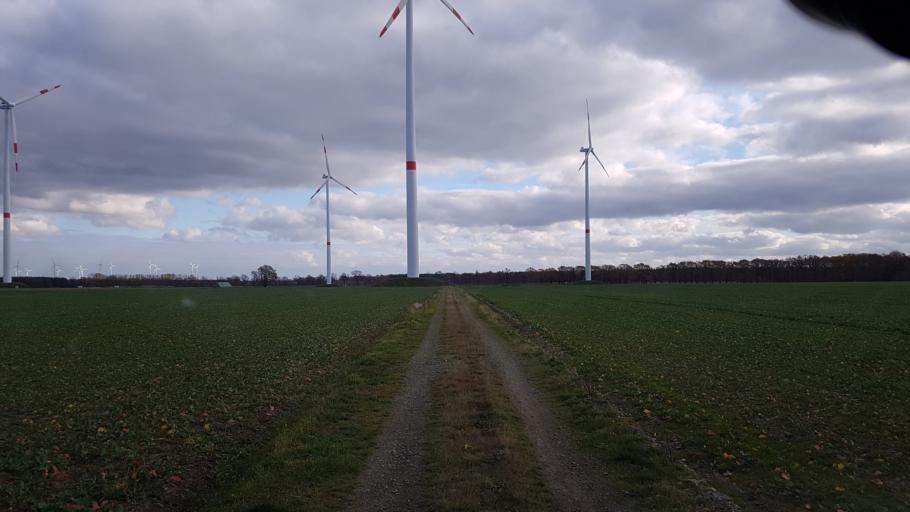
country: DE
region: Brandenburg
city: Sallgast
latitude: 51.6004
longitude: 13.8807
